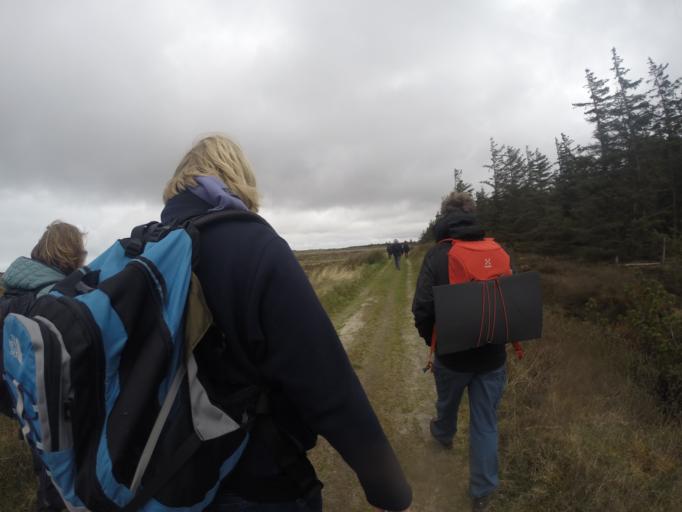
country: DK
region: North Denmark
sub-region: Thisted Kommune
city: Hurup
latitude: 56.9047
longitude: 8.3436
